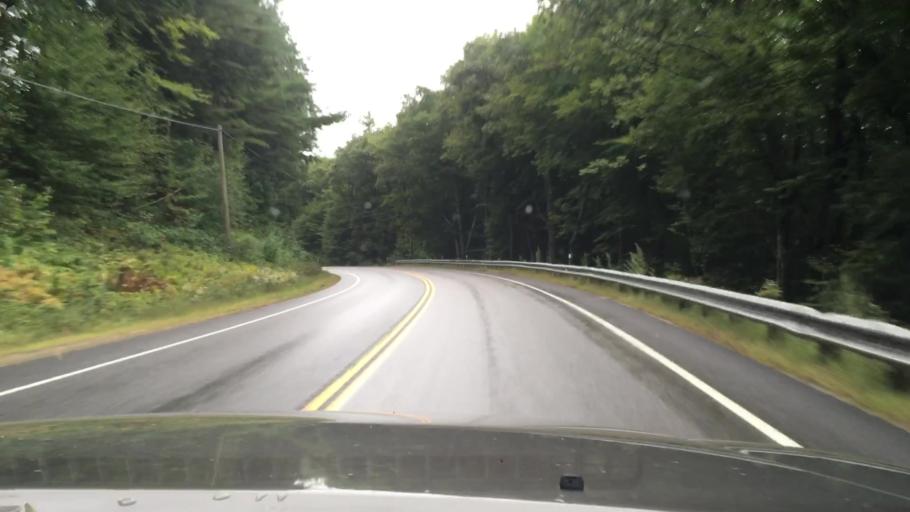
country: US
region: New Hampshire
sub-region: Hillsborough County
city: Antrim
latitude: 43.0768
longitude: -71.9862
